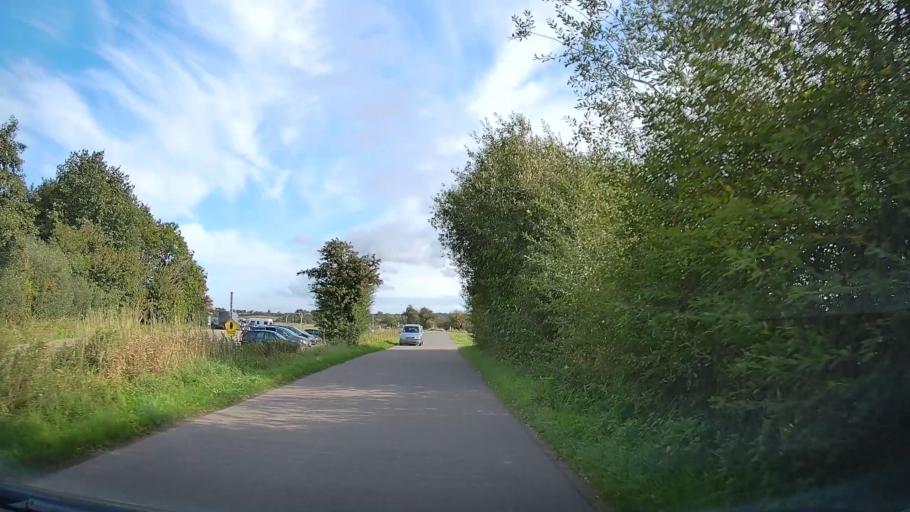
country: DE
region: Schleswig-Holstein
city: Steinberg
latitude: 54.7969
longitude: 9.7661
